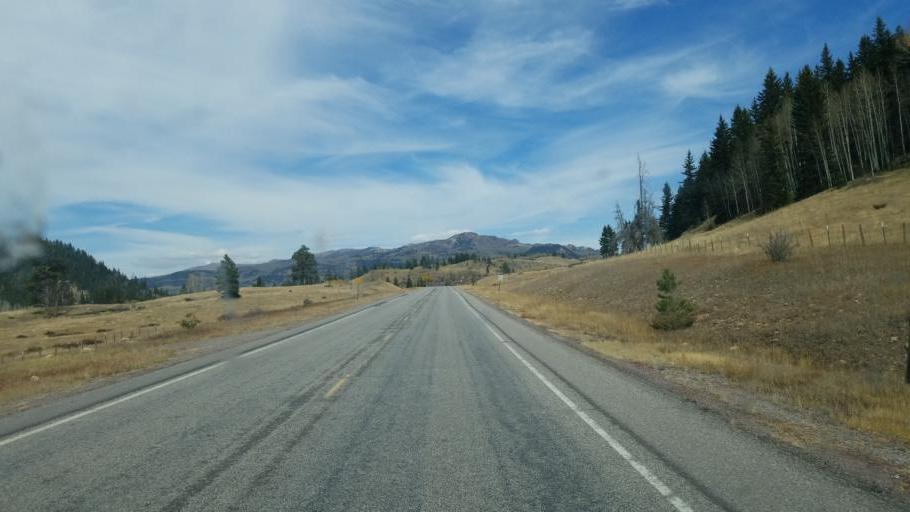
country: US
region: New Mexico
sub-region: Rio Arriba County
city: Chama
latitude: 36.9487
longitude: -106.5431
